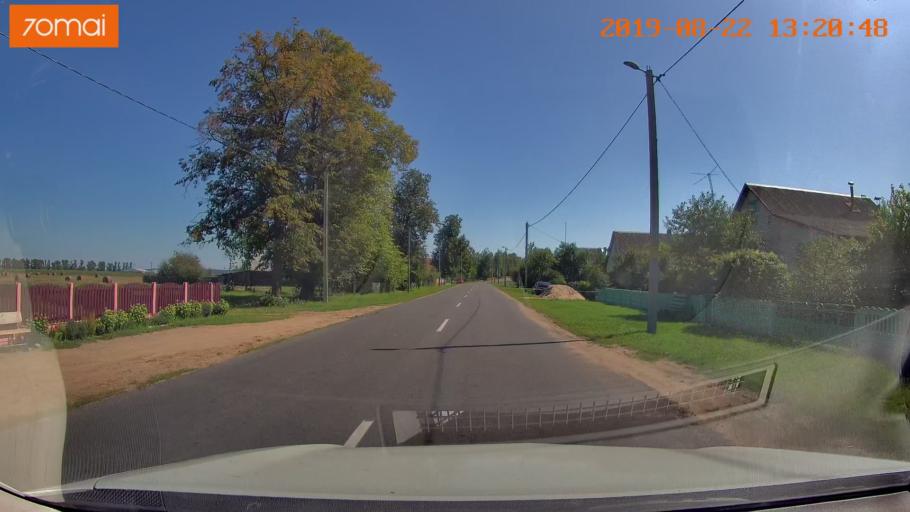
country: BY
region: Minsk
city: Urechcha
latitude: 53.2279
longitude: 27.9730
